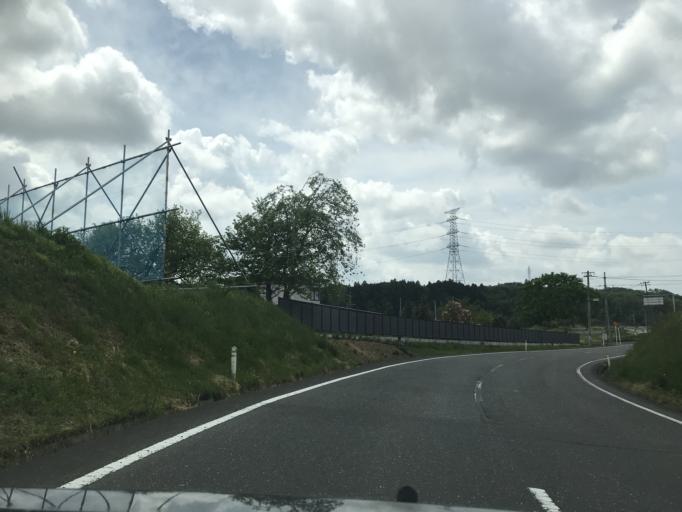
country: JP
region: Iwate
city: Ichinoseki
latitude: 38.8148
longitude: 141.0215
